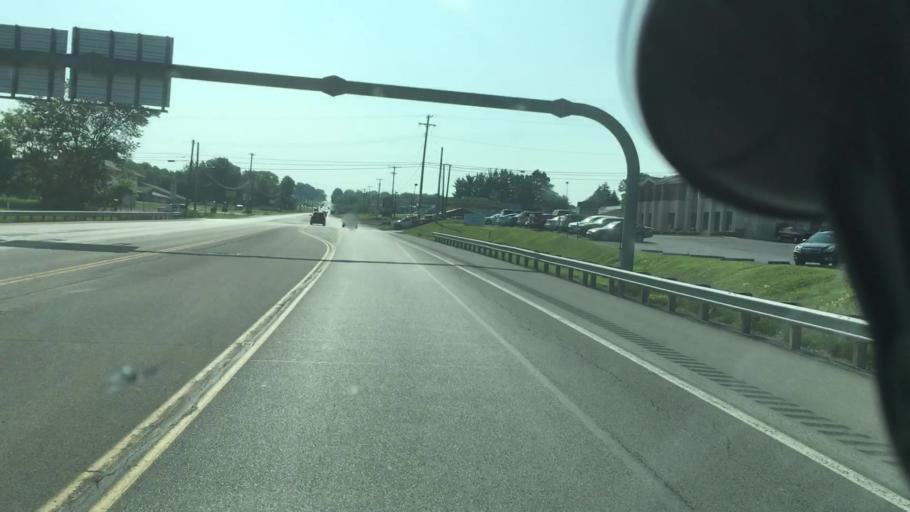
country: US
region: Pennsylvania
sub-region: Lawrence County
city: New Castle
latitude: 40.9772
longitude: -80.2961
